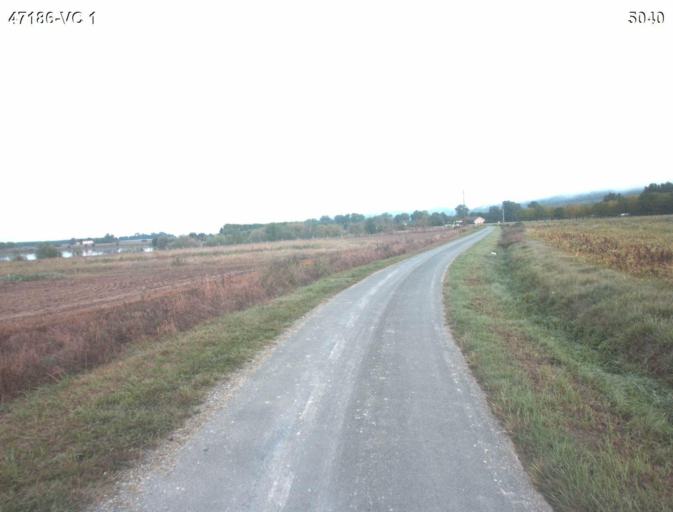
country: FR
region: Aquitaine
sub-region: Departement du Lot-et-Garonne
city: Port-Sainte-Marie
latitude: 44.2285
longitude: 0.4355
